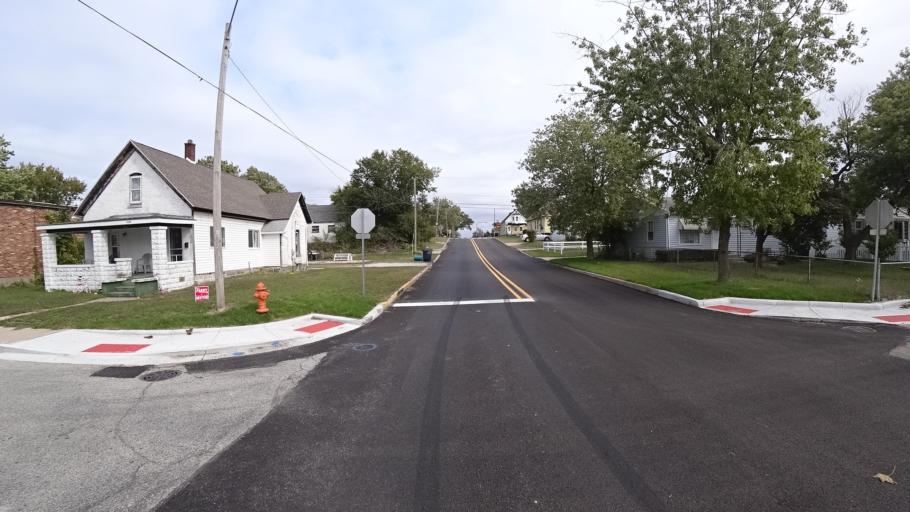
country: US
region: Indiana
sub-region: LaPorte County
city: Michigan City
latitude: 41.7047
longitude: -86.9050
